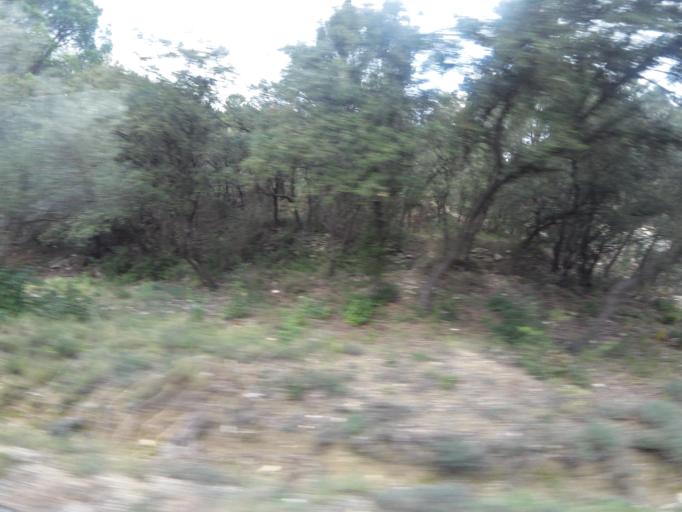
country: FR
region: Languedoc-Roussillon
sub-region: Departement du Gard
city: Clarensac
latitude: 43.8337
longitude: 4.1978
